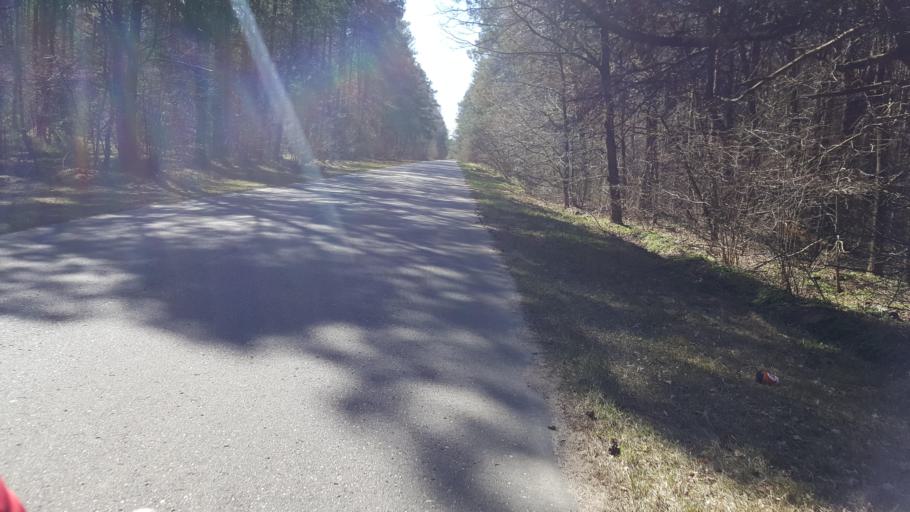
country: BY
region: Brest
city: Kamyanyets
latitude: 52.3026
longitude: 23.8423
